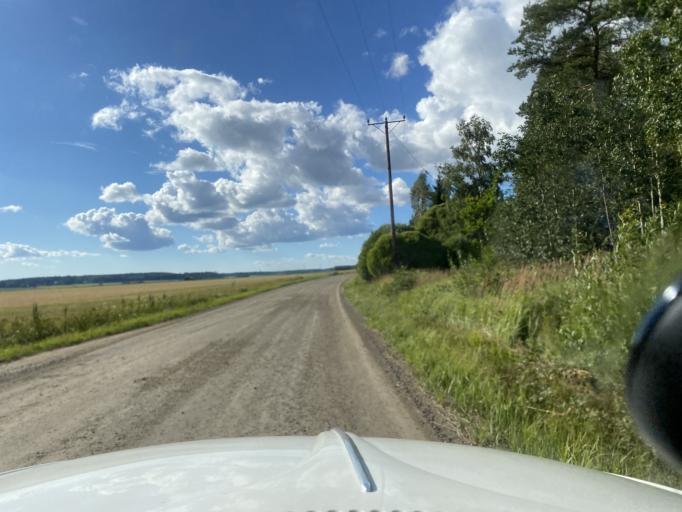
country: FI
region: Pirkanmaa
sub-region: Lounais-Pirkanmaa
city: Punkalaidun
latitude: 61.1414
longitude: 23.2058
